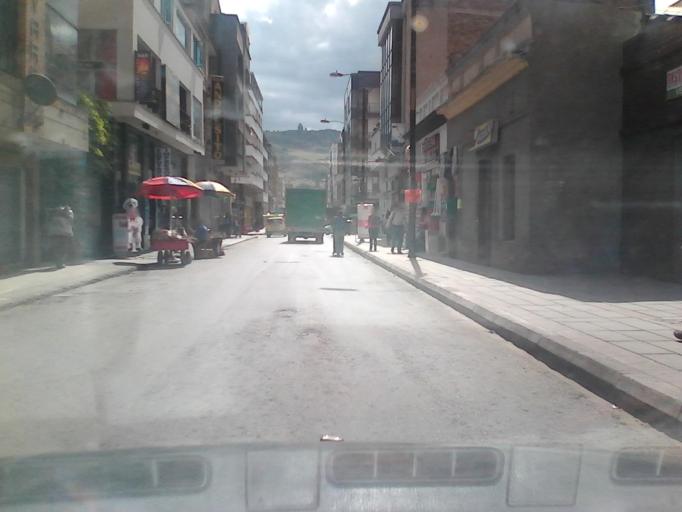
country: CO
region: Boyaca
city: Duitama
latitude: 5.8258
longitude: -73.0335
